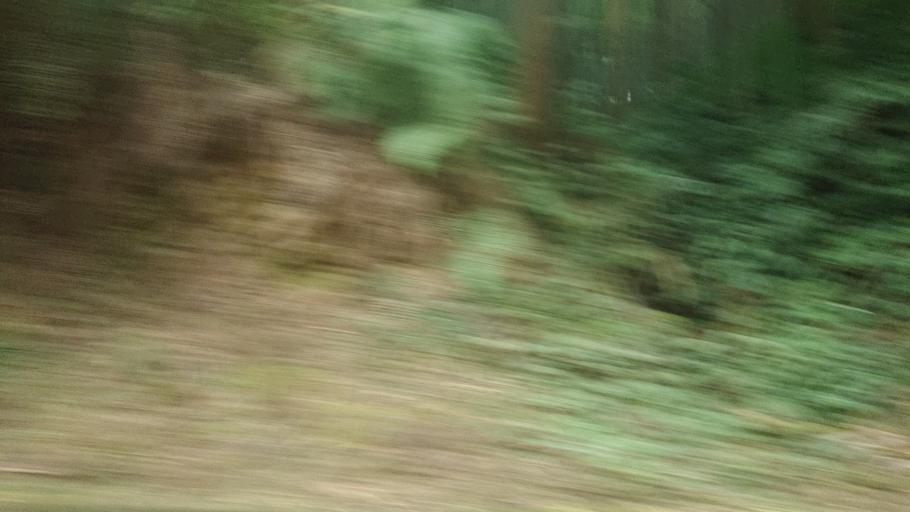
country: TW
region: Taiwan
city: Lugu
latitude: 23.6239
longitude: 120.7156
